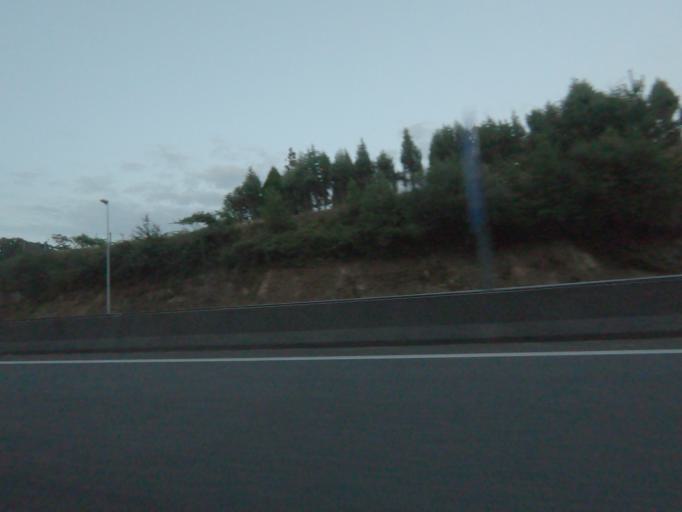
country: ES
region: Galicia
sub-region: Provincia de Pontevedra
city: Tui
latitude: 42.0687
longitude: -8.6341
